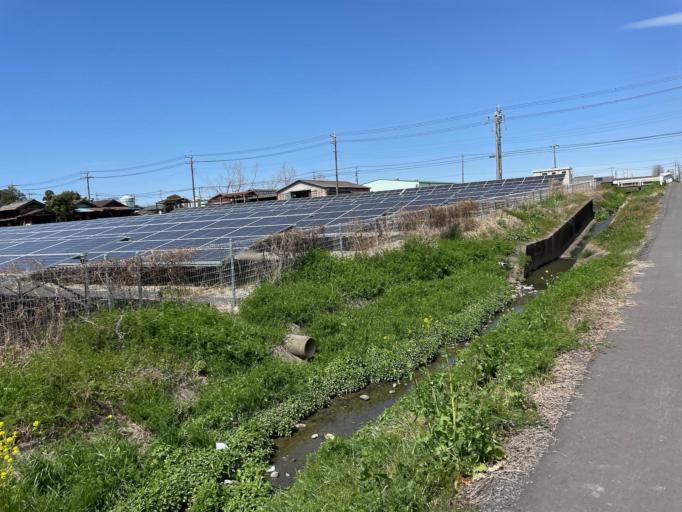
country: JP
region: Saitama
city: Yorii
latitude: 36.1207
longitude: 139.2434
